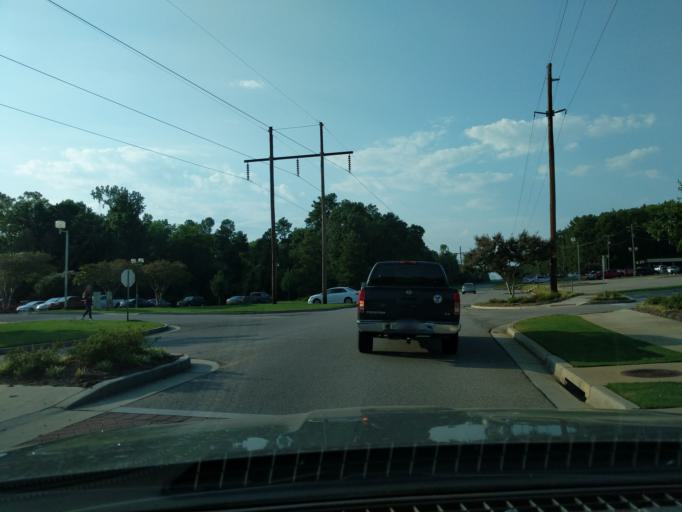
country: US
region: South Carolina
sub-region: Aiken County
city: North Augusta
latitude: 33.4997
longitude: -81.9866
